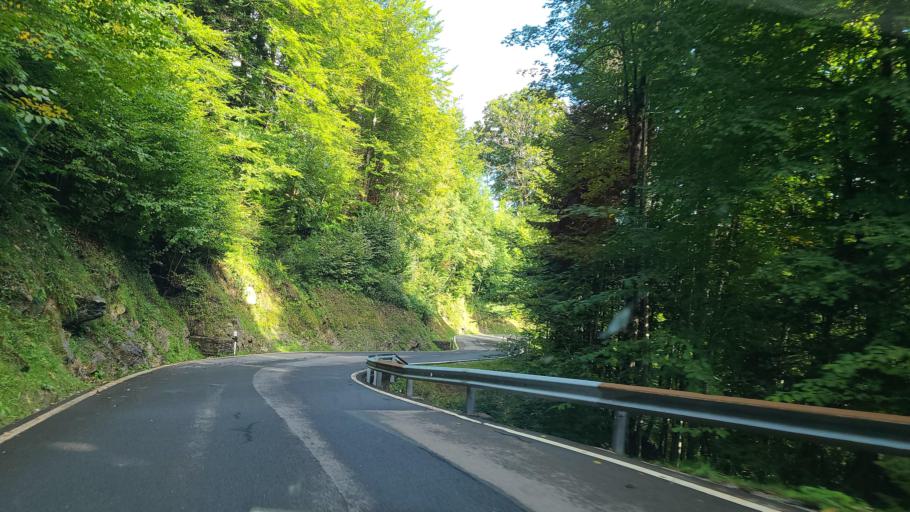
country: CH
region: Schwyz
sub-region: Bezirk March
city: Vorderthal
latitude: 47.1320
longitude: 8.8745
